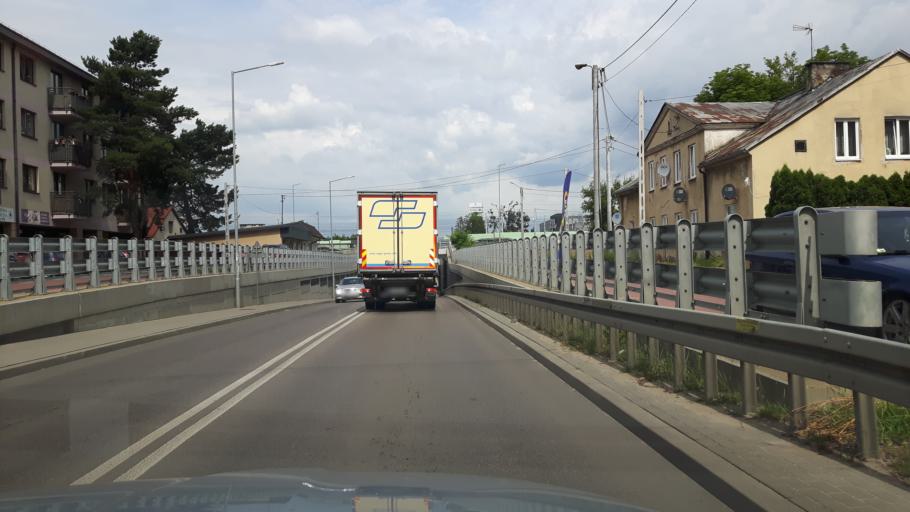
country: PL
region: Masovian Voivodeship
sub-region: Powiat wolominski
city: Nowe Lipiny
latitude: 52.3539
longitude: 21.2586
